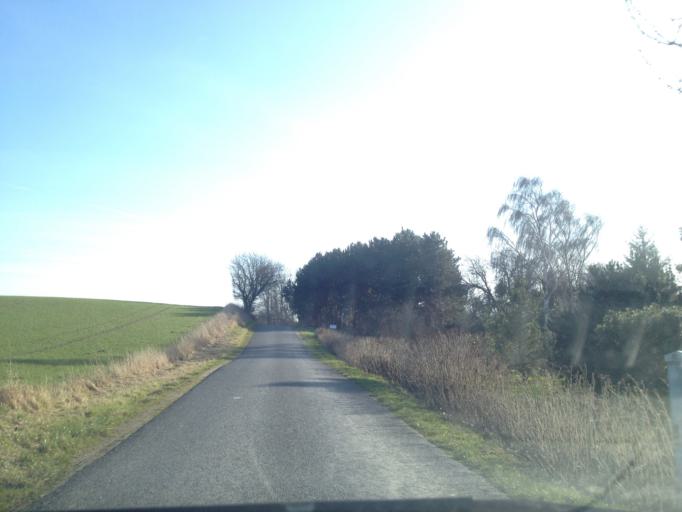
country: DK
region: South Denmark
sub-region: Kerteminde Kommune
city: Munkebo
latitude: 55.5681
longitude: 10.6110
